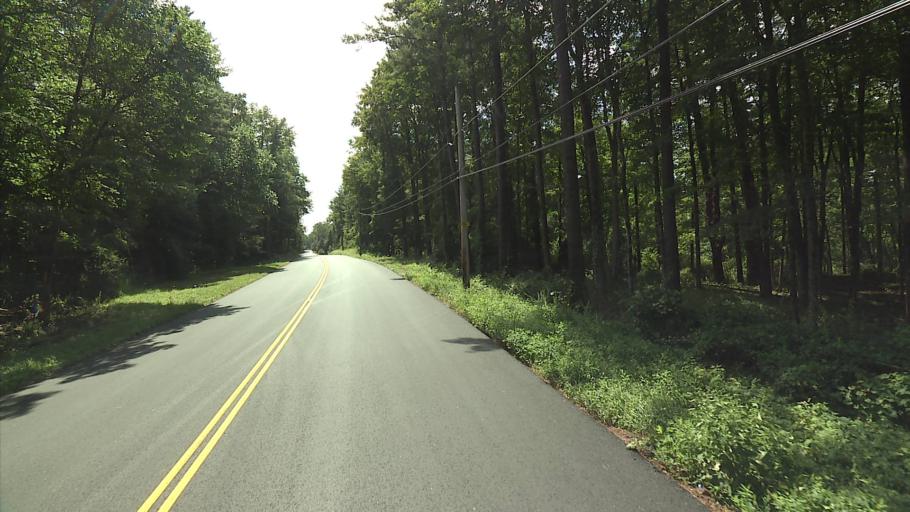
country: US
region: Connecticut
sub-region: Litchfield County
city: Canaan
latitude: 41.9985
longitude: -73.3600
